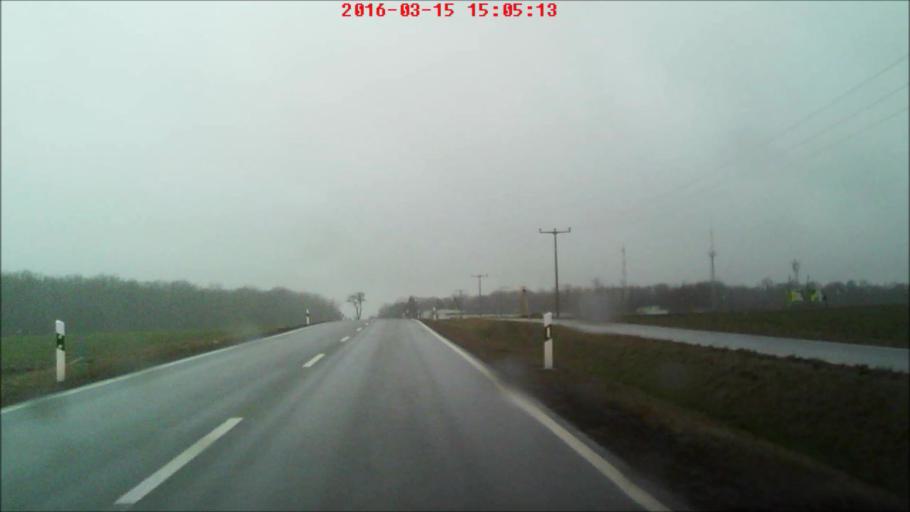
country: DE
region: Thuringia
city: Rockhausen
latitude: 50.9305
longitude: 11.0449
